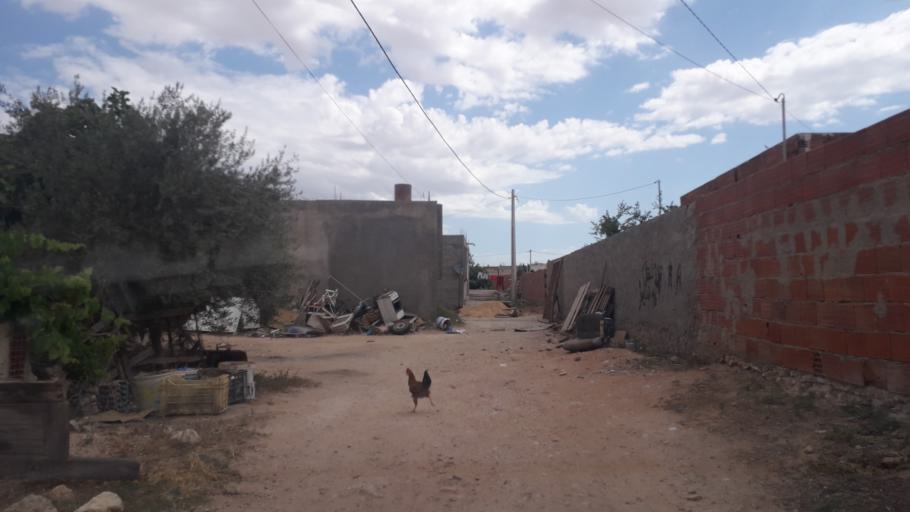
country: TN
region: Safaqis
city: Al Qarmadah
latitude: 34.8399
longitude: 10.7759
